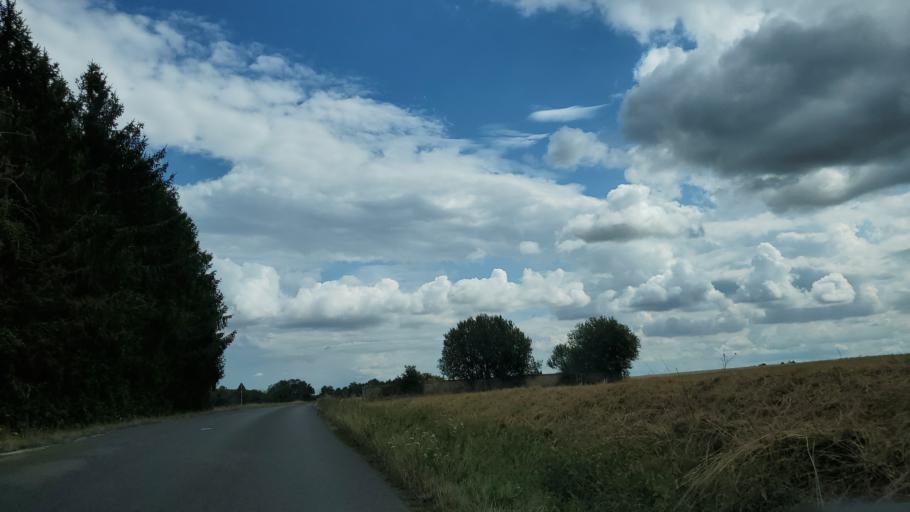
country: FR
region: Ile-de-France
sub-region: Departement de Seine-et-Marne
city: Mouroux
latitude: 48.8411
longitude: 3.0290
